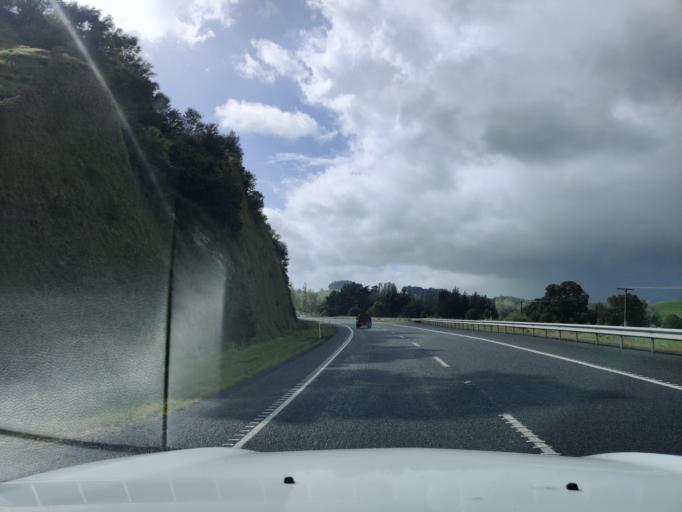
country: NZ
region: Waikato
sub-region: Matamata-Piako District
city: Matamata
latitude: -37.9530
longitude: 175.6773
